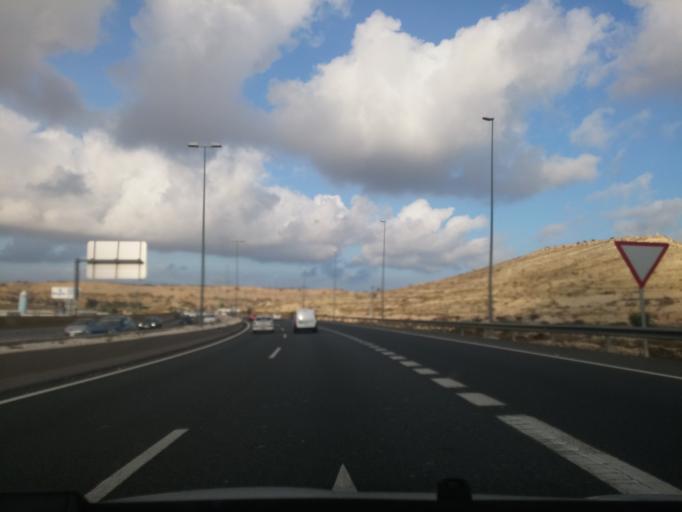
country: ES
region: Valencia
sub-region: Provincia de Alicante
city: Alicante
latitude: 38.3841
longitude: -0.4850
